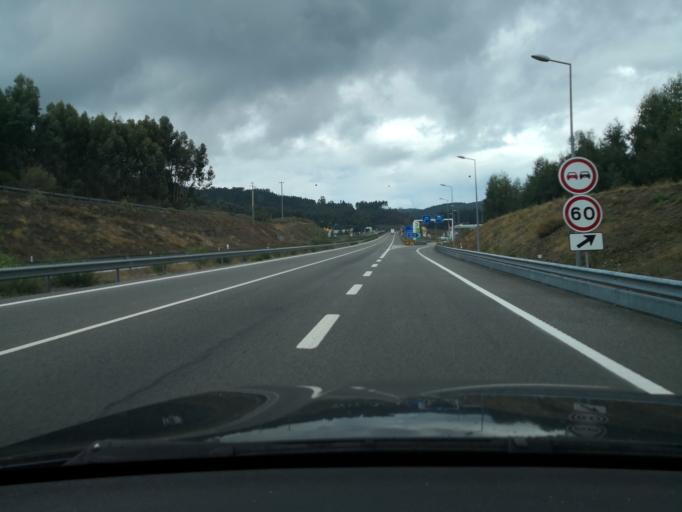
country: PT
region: Porto
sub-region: Lousada
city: Lousada
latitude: 41.2994
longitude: -8.2637
